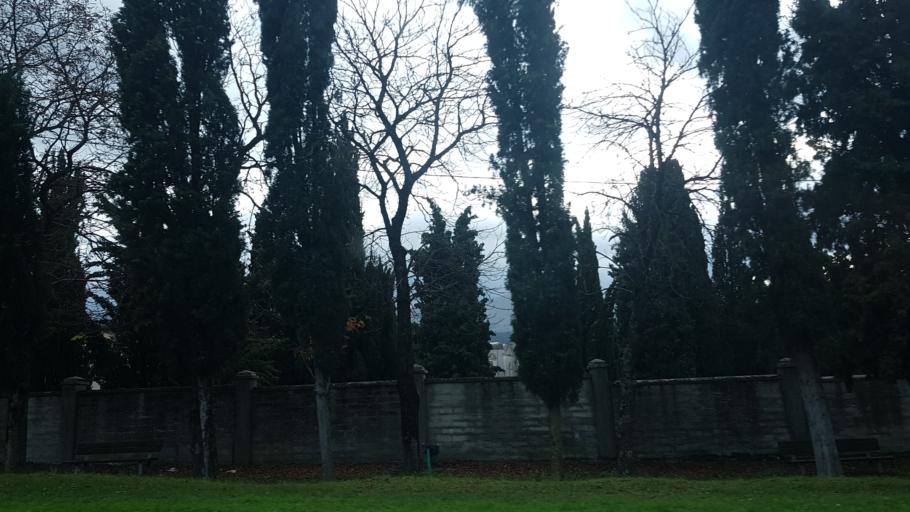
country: IT
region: Abruzzo
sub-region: Provincia dell' Aquila
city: L'Aquila
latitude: 42.3524
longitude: 13.4147
